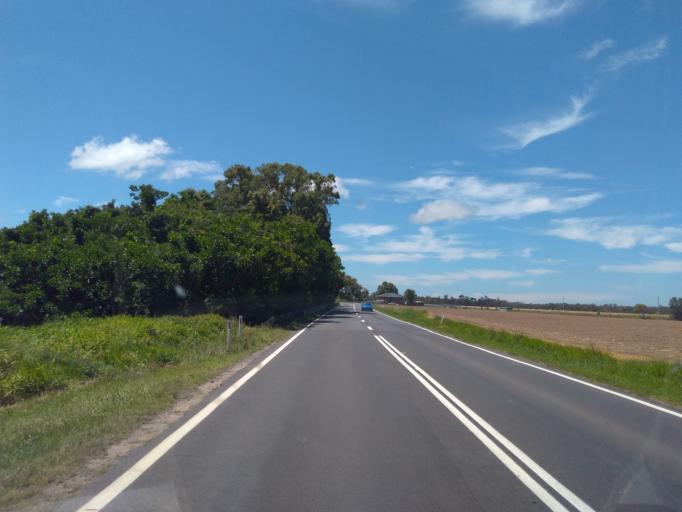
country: AU
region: New South Wales
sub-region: Clarence Valley
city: Maclean
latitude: -29.4823
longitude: 153.2019
